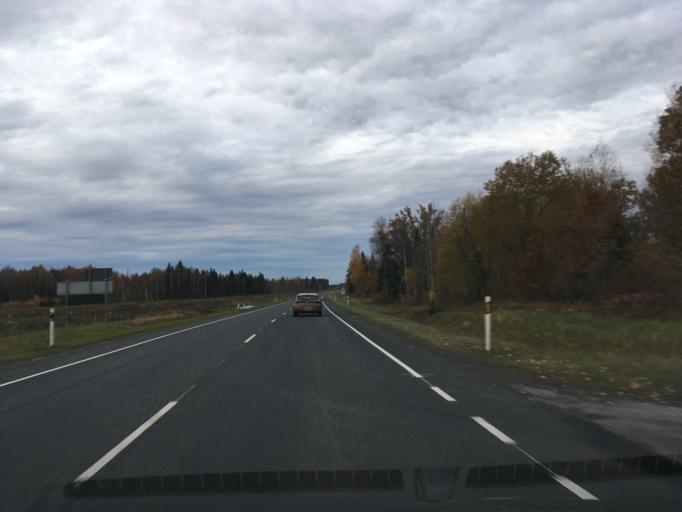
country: EE
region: Harju
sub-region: Nissi vald
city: Turba
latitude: 58.9408
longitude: 24.0890
